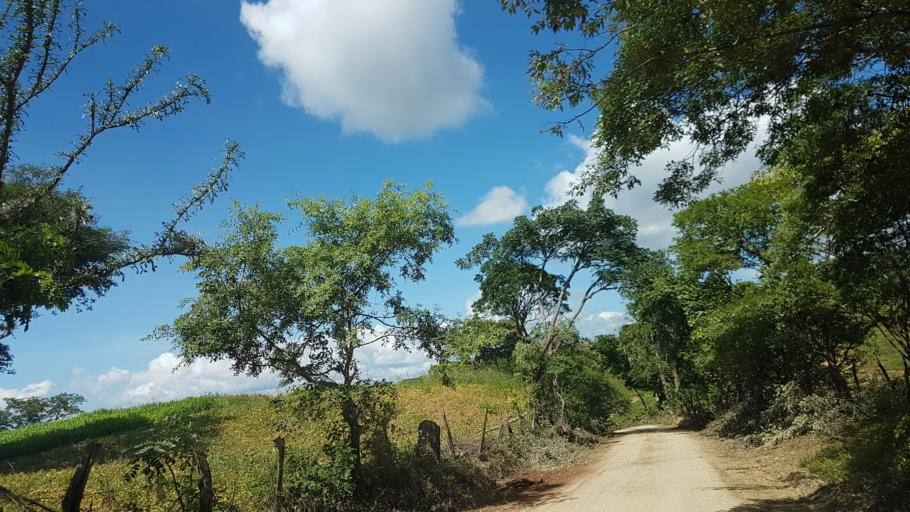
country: HN
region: El Paraiso
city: Santa Cruz
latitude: 13.7341
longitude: -86.6957
